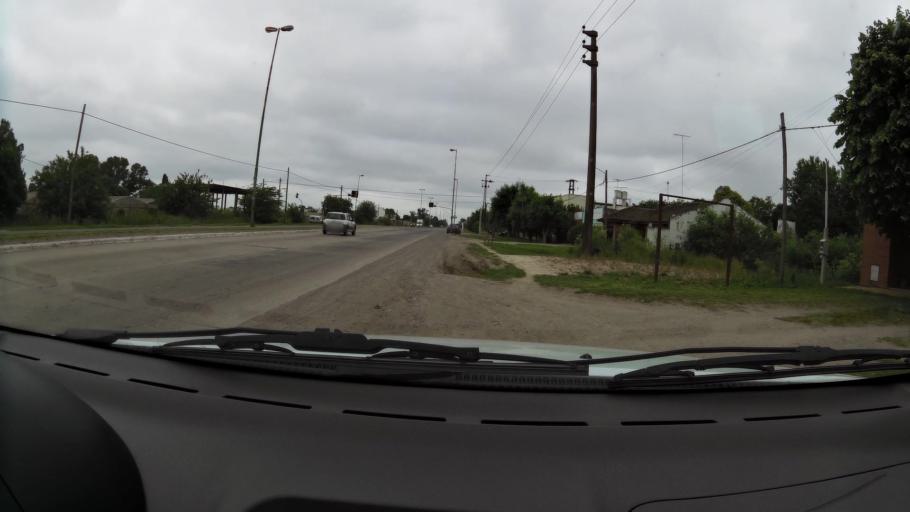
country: AR
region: Buenos Aires
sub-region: Partido de La Plata
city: La Plata
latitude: -35.0233
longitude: -58.0789
